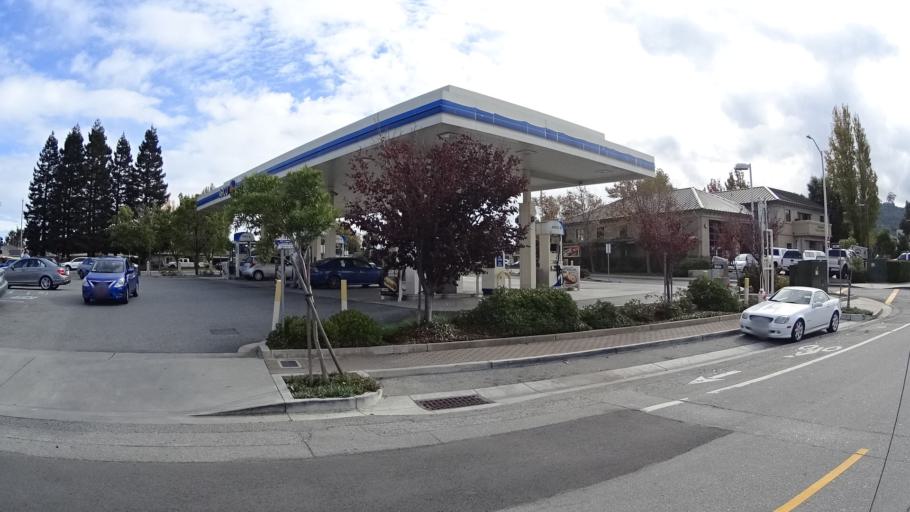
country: US
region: California
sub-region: San Mateo County
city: Belmont
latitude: 37.5235
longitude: -122.2737
